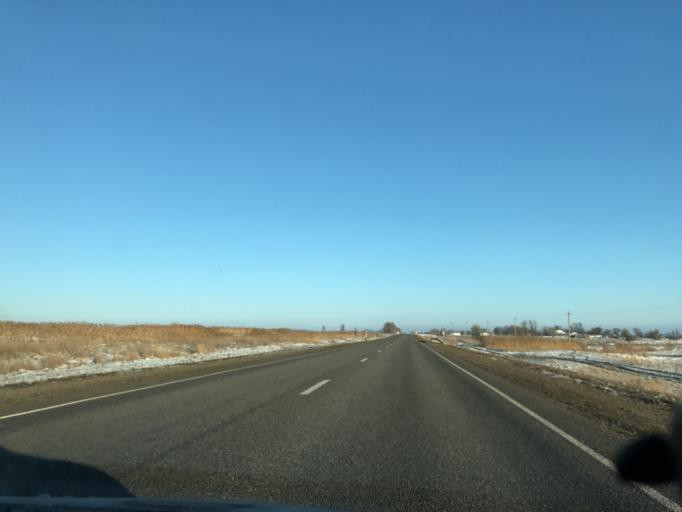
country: RU
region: Stavropol'skiy
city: Bezopasnoye
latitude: 45.5838
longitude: 41.9462
